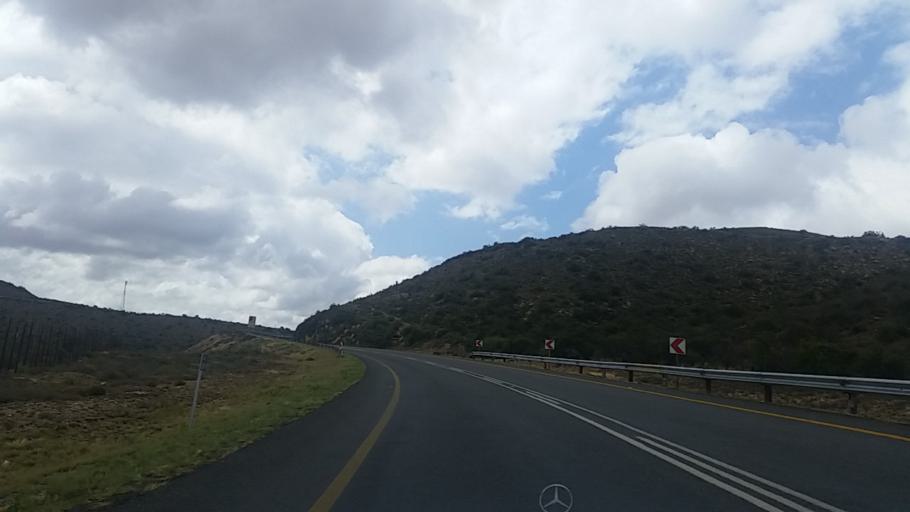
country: ZA
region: Eastern Cape
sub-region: Cacadu District Municipality
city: Graaff-Reinet
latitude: -32.1168
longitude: 24.6084
